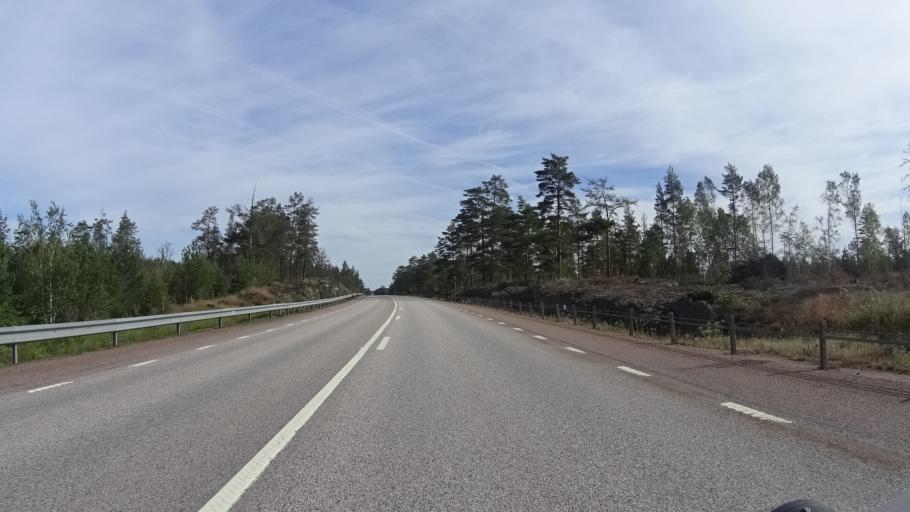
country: SE
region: Kalmar
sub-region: Oskarshamns Kommun
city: Oskarshamn
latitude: 57.4603
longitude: 16.5165
